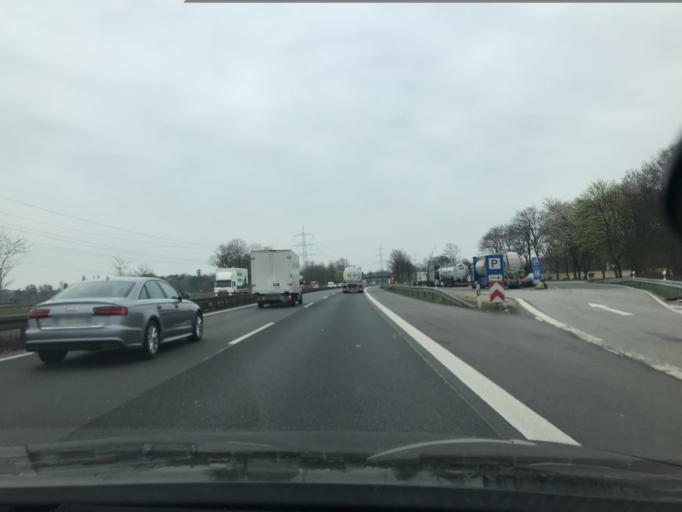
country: DE
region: North Rhine-Westphalia
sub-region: Regierungsbezirk Dusseldorf
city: Viersen
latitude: 51.2181
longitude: 6.4007
